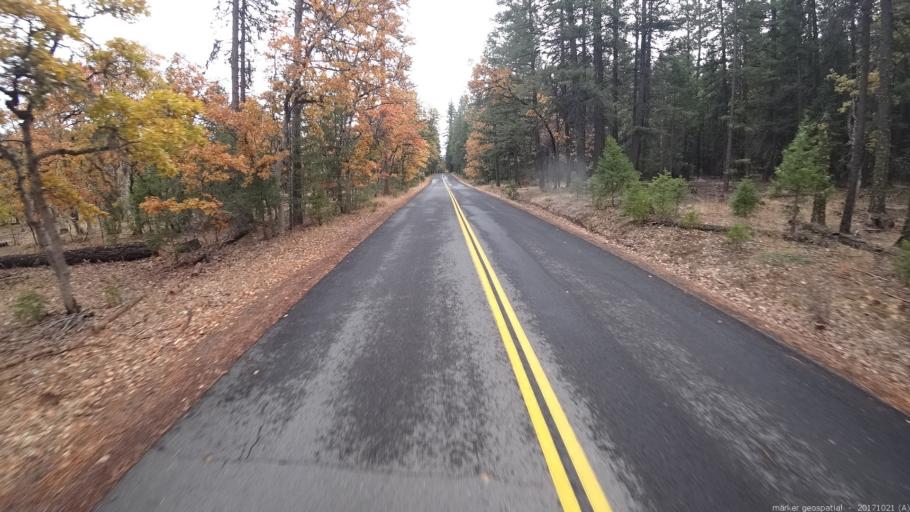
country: US
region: California
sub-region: Shasta County
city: Burney
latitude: 41.0174
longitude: -121.6604
